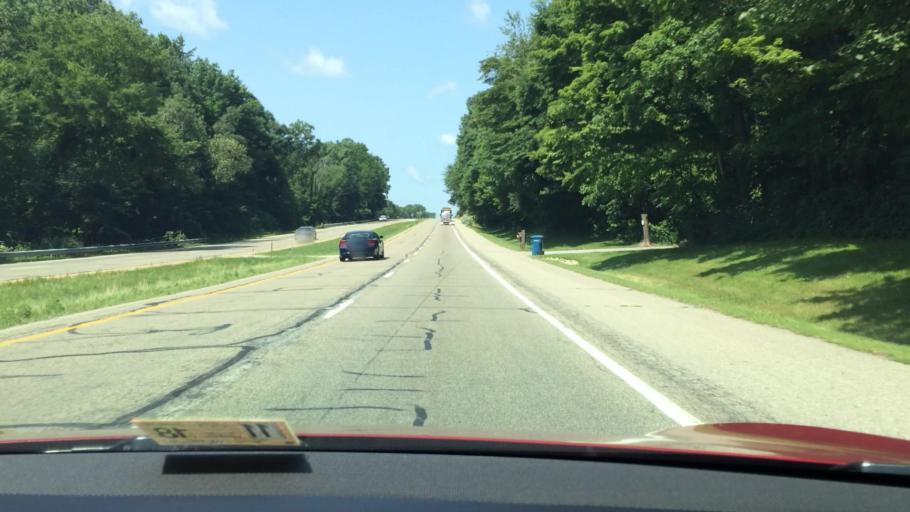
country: US
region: Indiana
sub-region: LaPorte County
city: Hudson Lake
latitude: 41.6726
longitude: -86.5420
